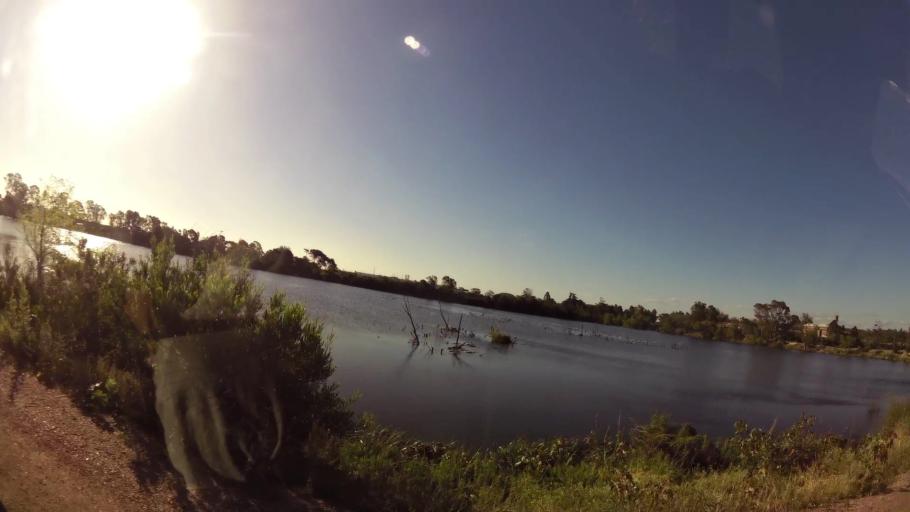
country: UY
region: Canelones
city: Paso de Carrasco
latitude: -34.8624
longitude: -56.0422
